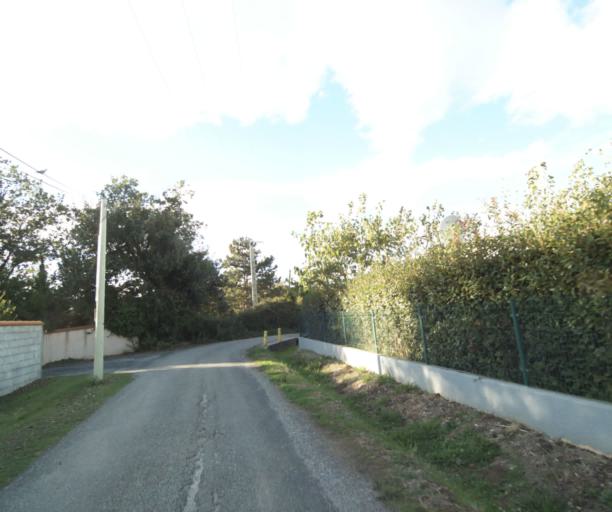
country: FR
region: Languedoc-Roussillon
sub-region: Departement des Pyrenees-Orientales
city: Argelers
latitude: 42.5692
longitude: 3.0113
